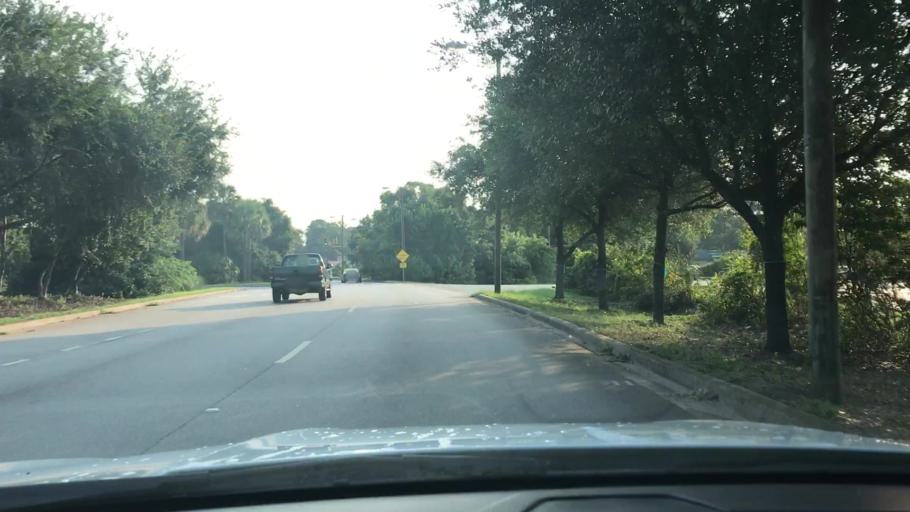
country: US
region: South Carolina
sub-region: Charleston County
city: North Charleston
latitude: 32.8165
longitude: -79.9944
